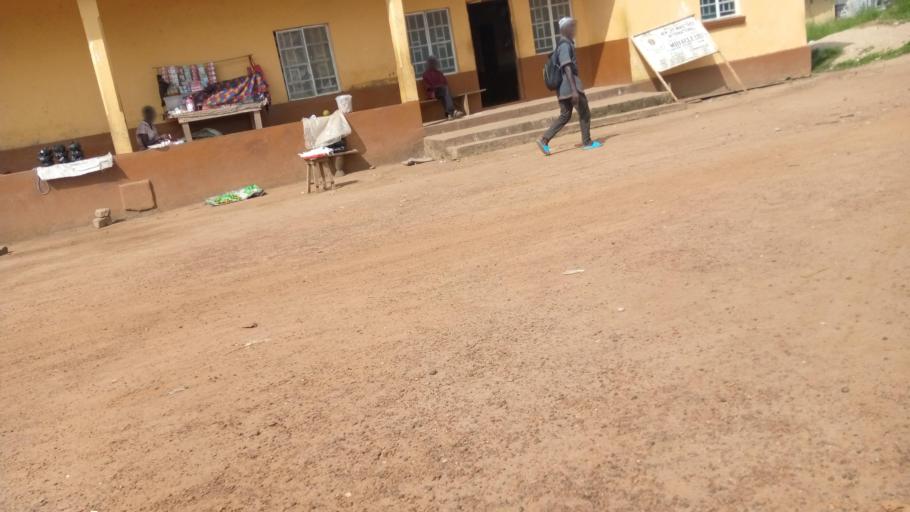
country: SL
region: Southern Province
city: Pujehun
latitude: 7.3585
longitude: -11.7226
